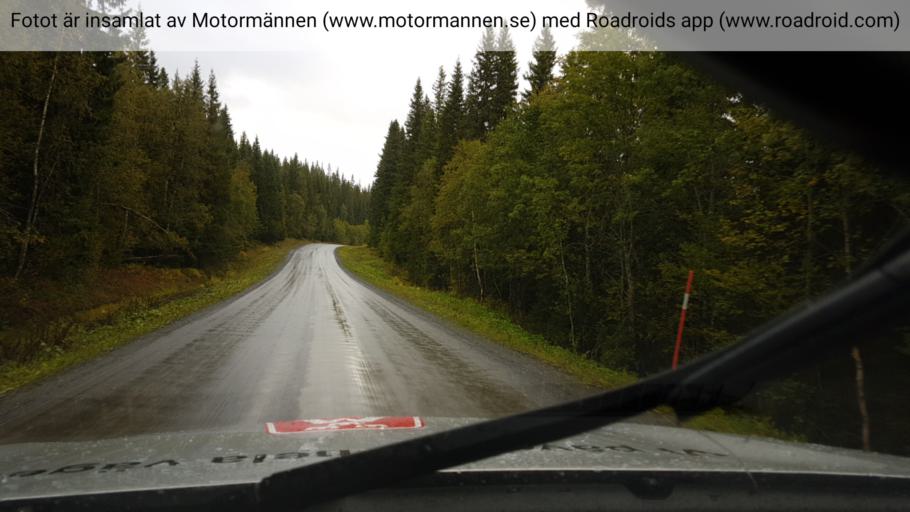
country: SE
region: Jaemtland
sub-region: Are Kommun
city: Are
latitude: 63.6782
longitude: 12.8920
